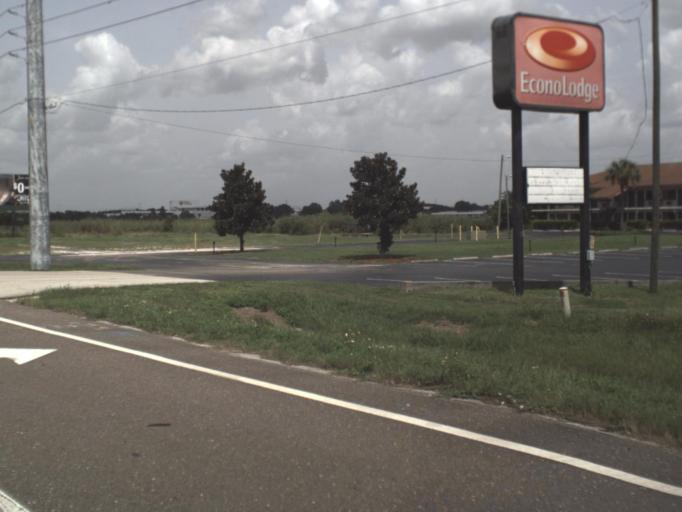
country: US
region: Florida
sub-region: Highlands County
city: Avon Park
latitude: 27.5604
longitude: -81.5116
